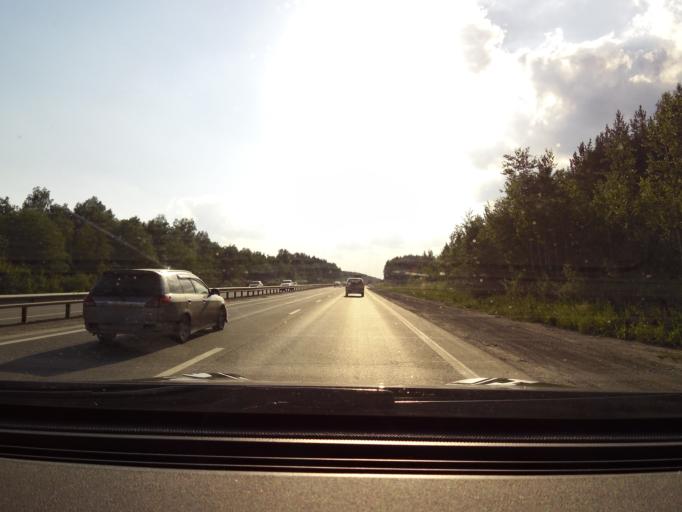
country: RU
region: Sverdlovsk
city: Severka
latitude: 56.8320
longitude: 60.3596
